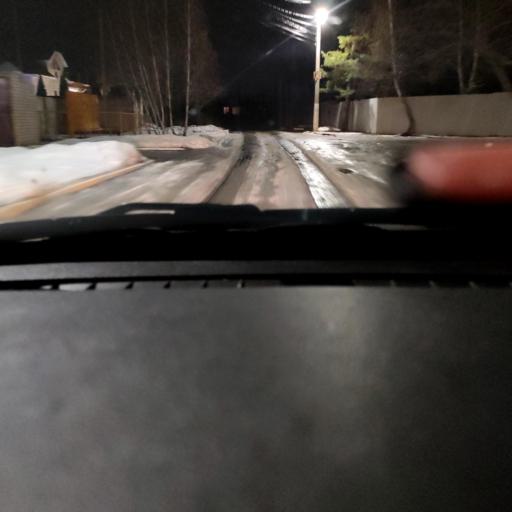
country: RU
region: Voronezj
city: Podgornoye
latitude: 51.7878
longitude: 39.1524
